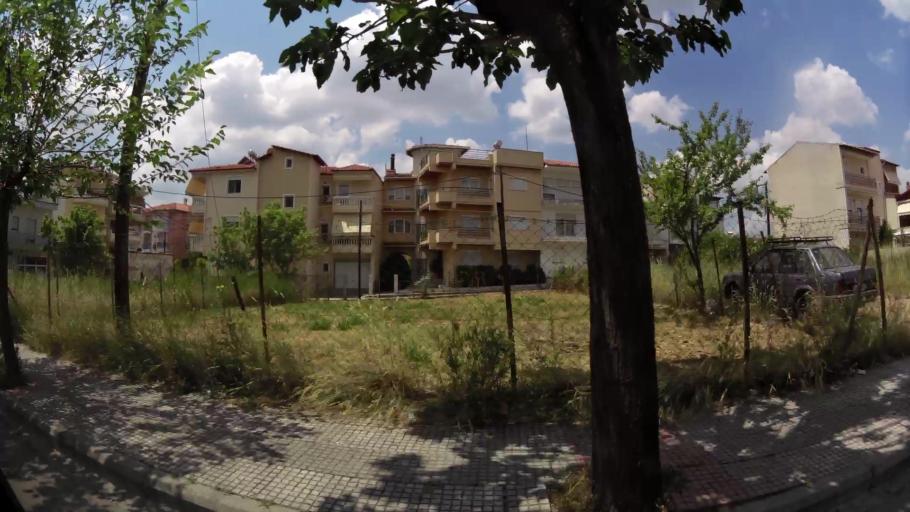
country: GR
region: West Macedonia
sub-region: Nomos Kozanis
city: Kozani
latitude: 40.2962
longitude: 21.7979
